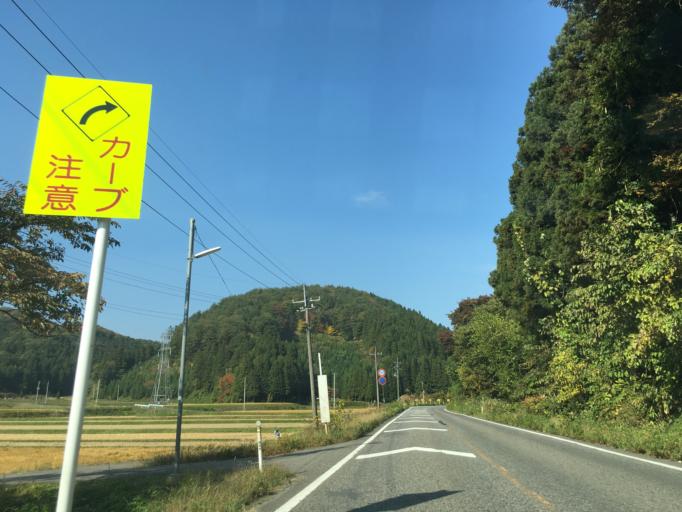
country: JP
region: Fukushima
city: Inawashiro
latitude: 37.3832
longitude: 140.1127
